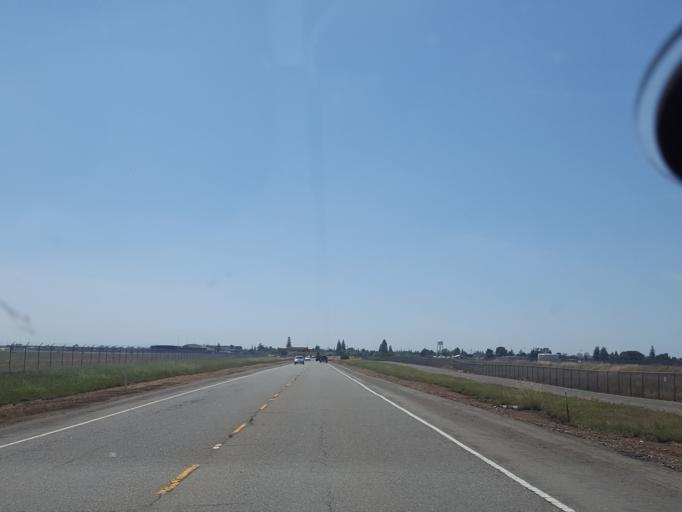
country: US
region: California
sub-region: Sacramento County
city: Rancho Cordova
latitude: 38.5676
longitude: -121.2766
